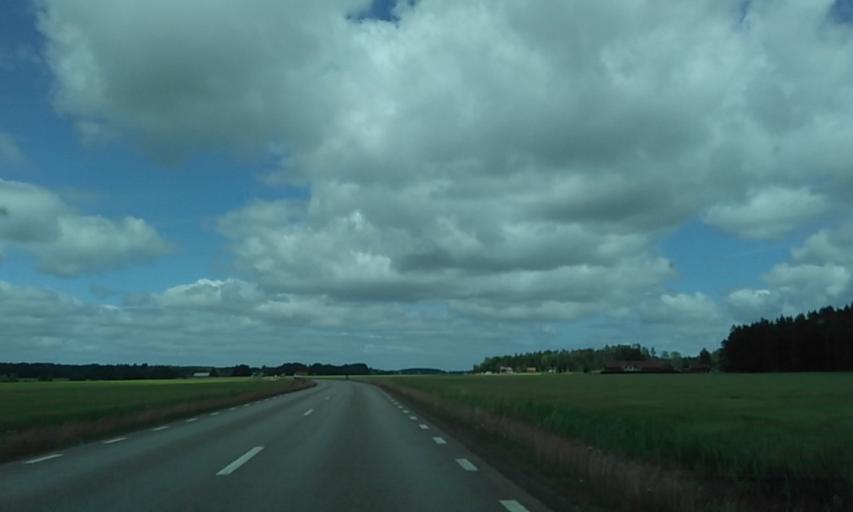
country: SE
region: Vaestra Goetaland
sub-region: Grastorps Kommun
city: Graestorp
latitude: 58.2802
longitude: 12.6749
